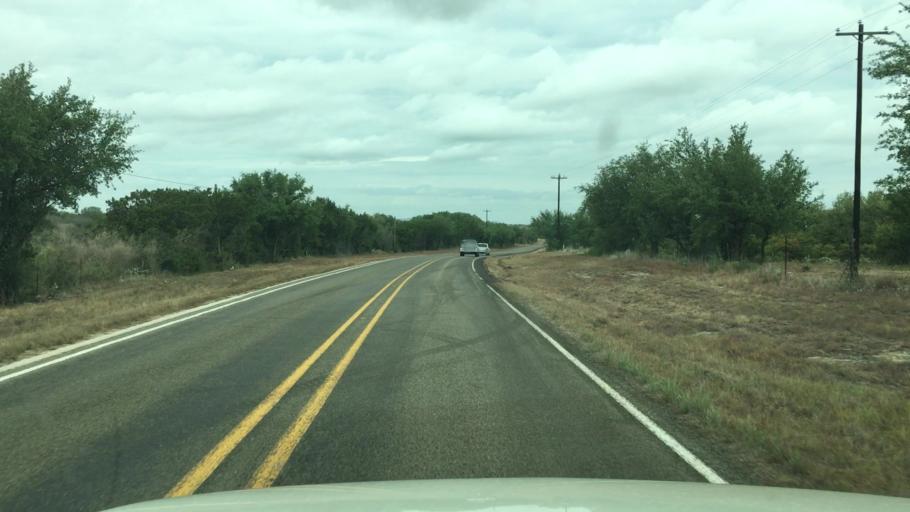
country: US
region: Texas
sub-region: Llano County
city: Horseshoe Bay
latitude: 30.4721
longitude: -98.4152
